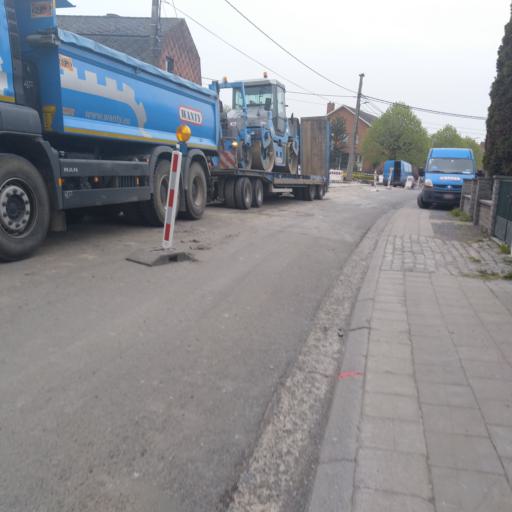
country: BE
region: Wallonia
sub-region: Province du Hainaut
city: Mons
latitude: 50.4575
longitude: 3.9664
